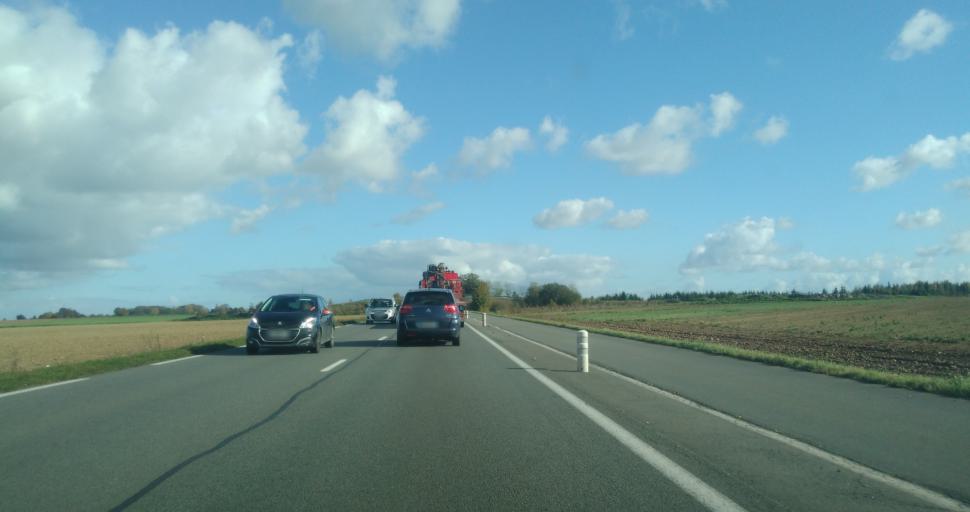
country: FR
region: Nord-Pas-de-Calais
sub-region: Departement du Pas-de-Calais
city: Anzin-Saint-Aubin
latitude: 50.3235
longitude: 2.7425
